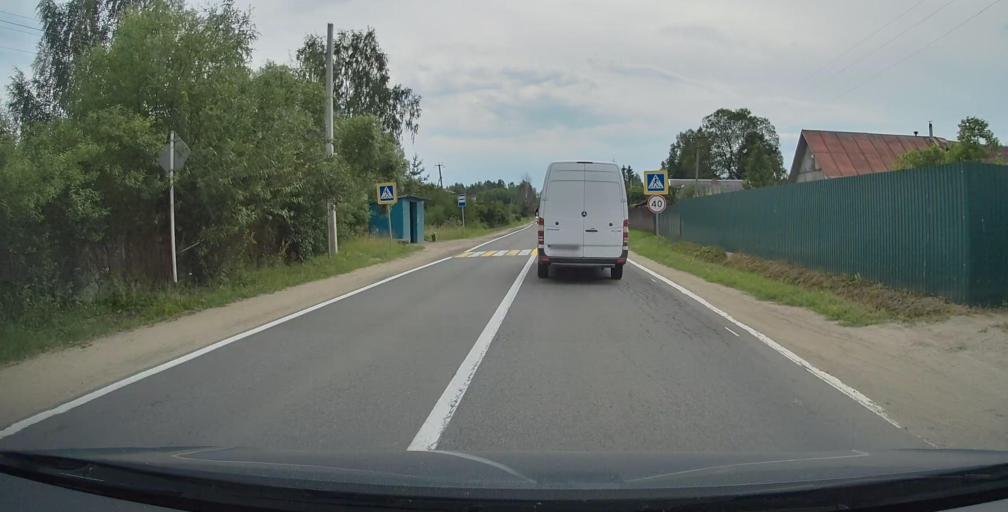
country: RU
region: Jaroslavl
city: Rybinsk
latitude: 57.9750
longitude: 38.7372
